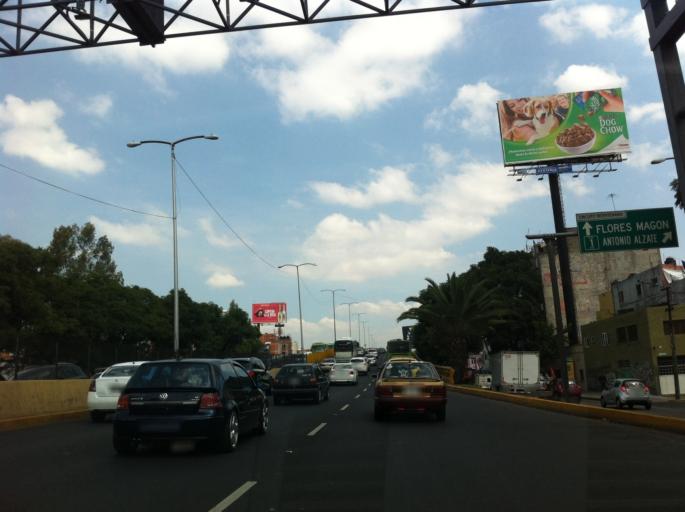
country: MX
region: Mexico City
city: Cuauhtemoc
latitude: 19.4457
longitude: -99.1652
